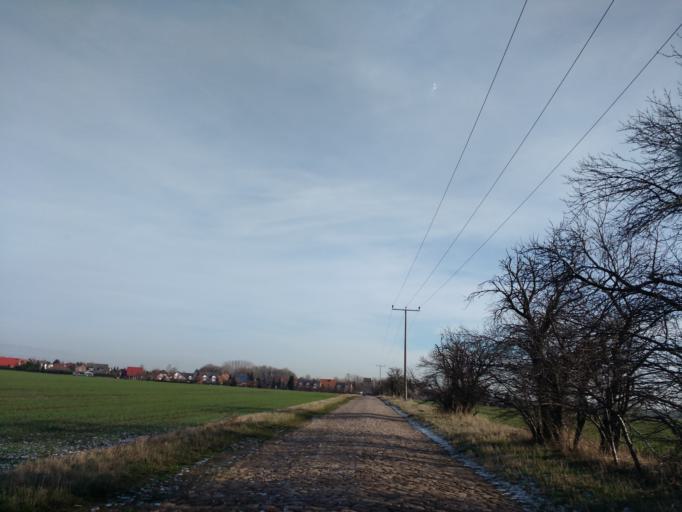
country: DE
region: Saxony-Anhalt
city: Braschwitz
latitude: 51.5349
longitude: 12.0532
